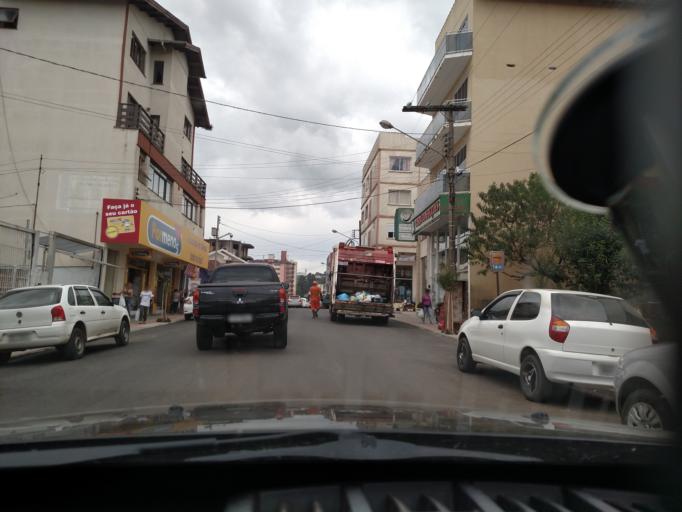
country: BR
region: Santa Catarina
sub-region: Sao Joaquim
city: Sao Joaquim
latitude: -28.2933
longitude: -49.9349
